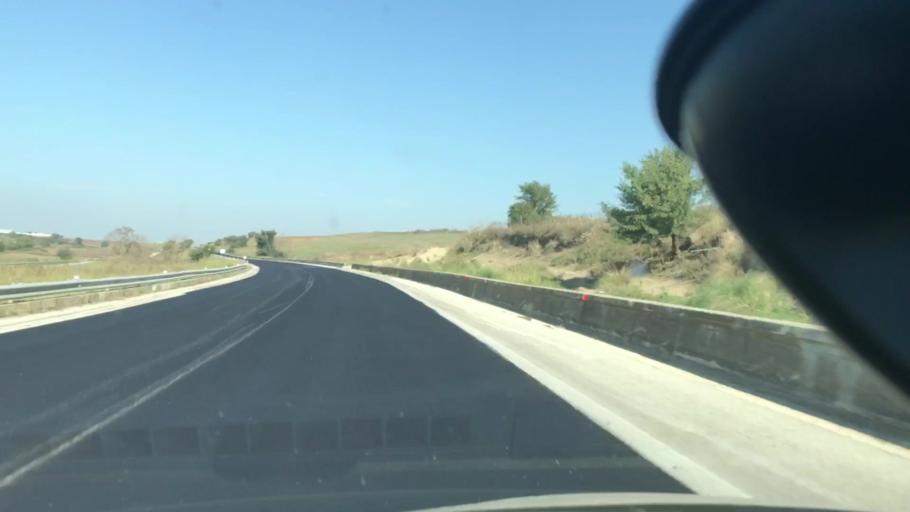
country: IT
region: Apulia
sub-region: Provincia di Barletta - Andria - Trani
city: Spinazzola
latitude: 40.9014
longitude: 16.1200
